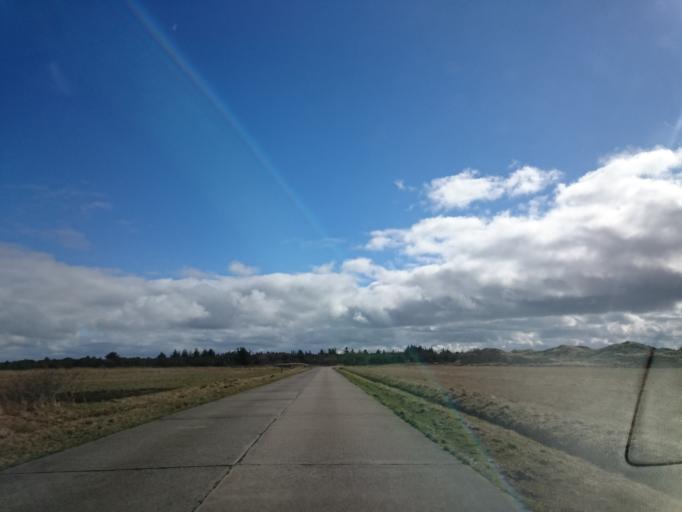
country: DK
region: North Denmark
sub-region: Frederikshavn Kommune
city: Skagen
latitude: 57.6584
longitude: 10.4084
